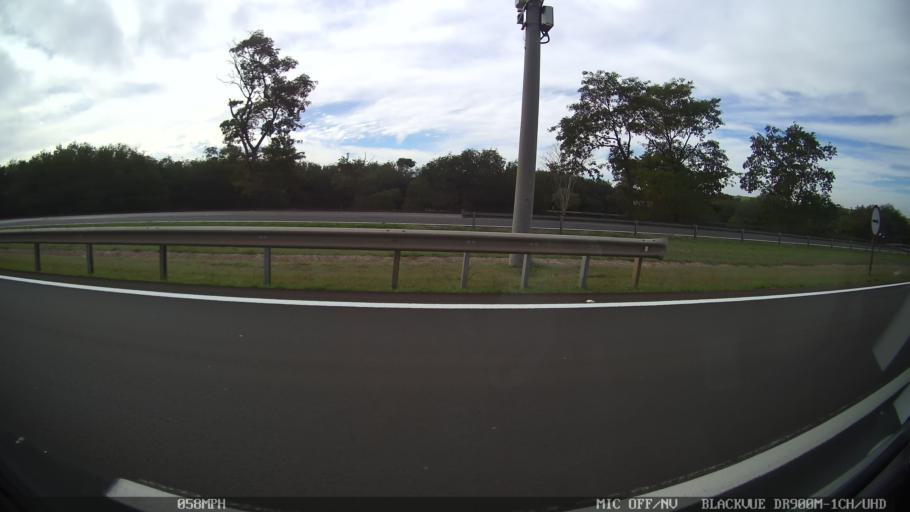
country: BR
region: Sao Paulo
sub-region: Taquaritinga
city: Taquaritinga
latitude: -21.4752
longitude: -48.5994
